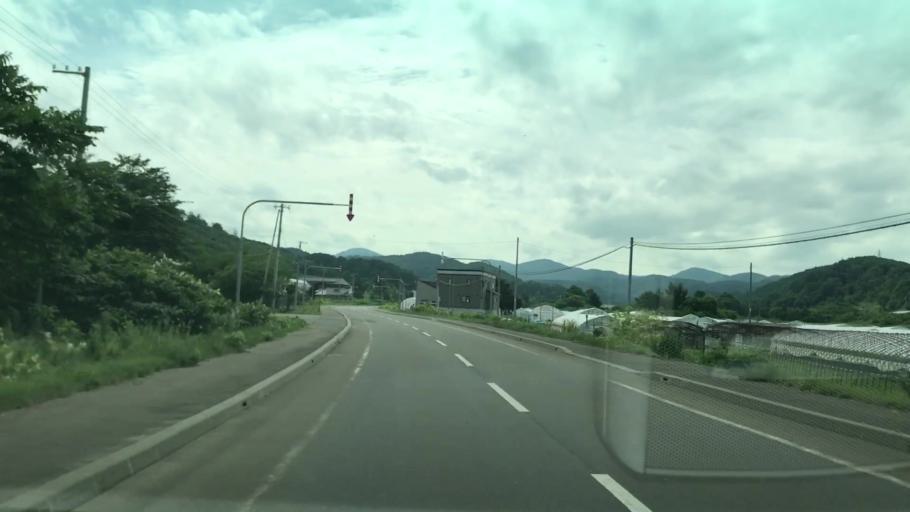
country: JP
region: Hokkaido
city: Yoichi
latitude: 43.1854
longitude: 140.8426
